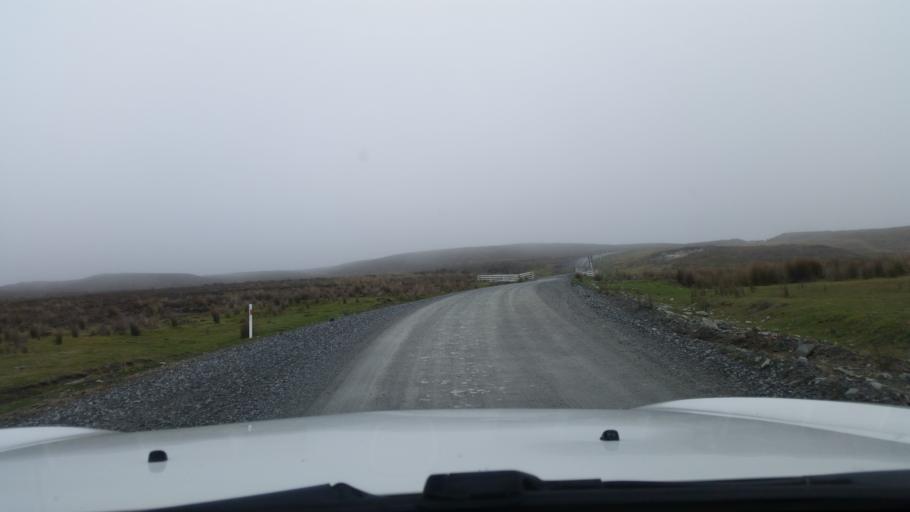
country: NZ
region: Chatham Islands
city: Waitangi
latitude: -43.7958
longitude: -176.6641
